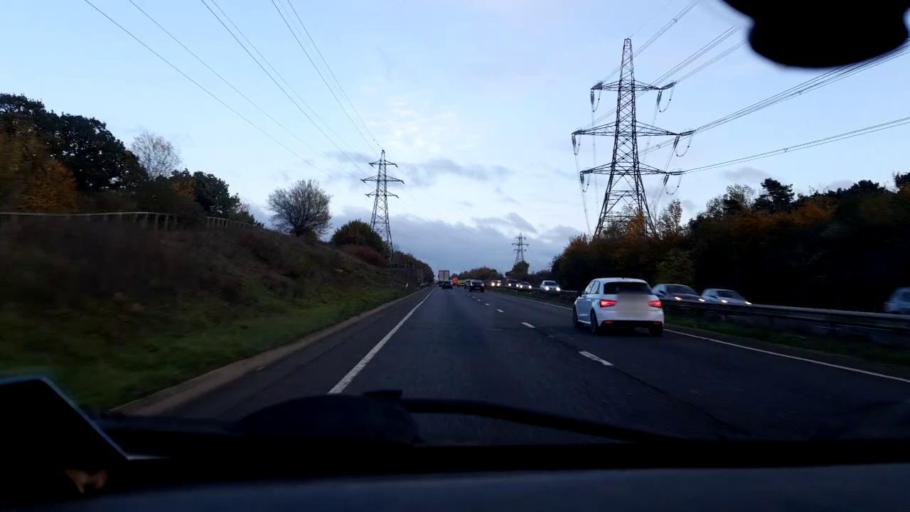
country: GB
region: England
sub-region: Norfolk
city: Cringleford
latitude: 52.5907
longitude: 1.2481
